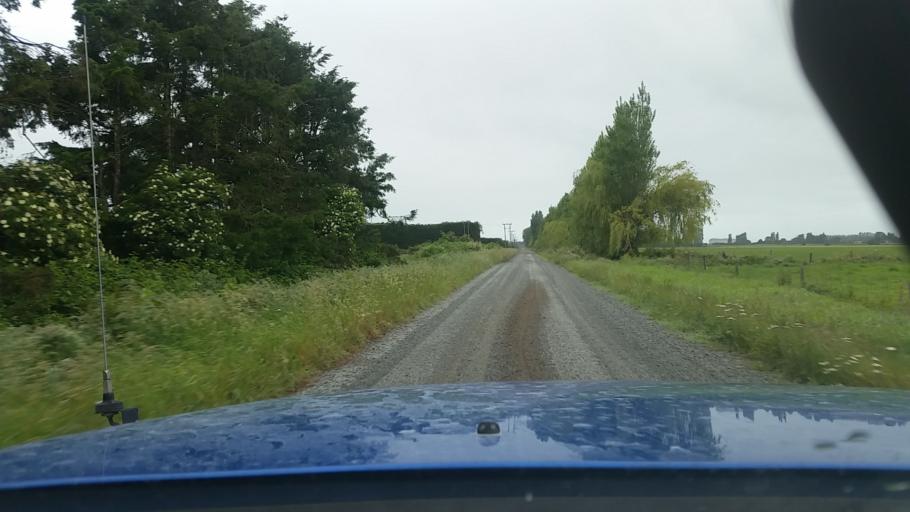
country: NZ
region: Canterbury
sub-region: Ashburton District
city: Tinwald
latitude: -44.0019
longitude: 171.6651
